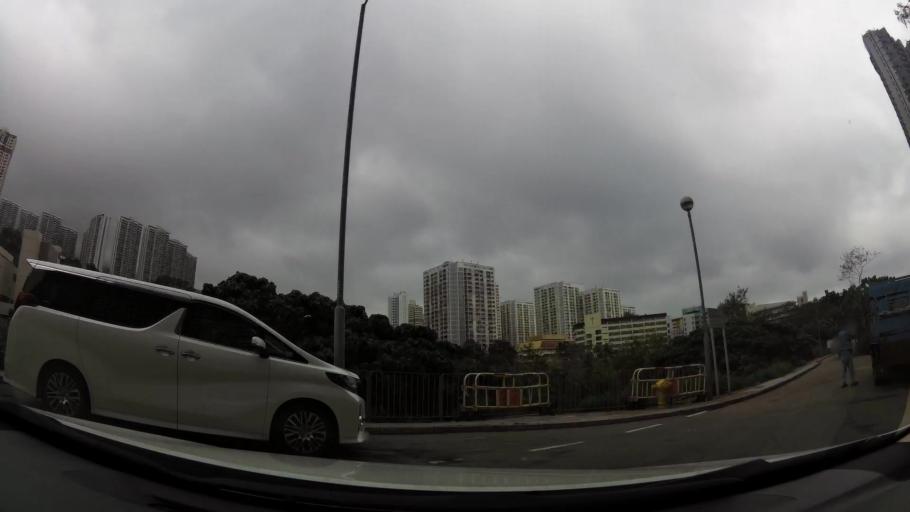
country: HK
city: Yung Shue Wan
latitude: 22.2554
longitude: 114.1340
